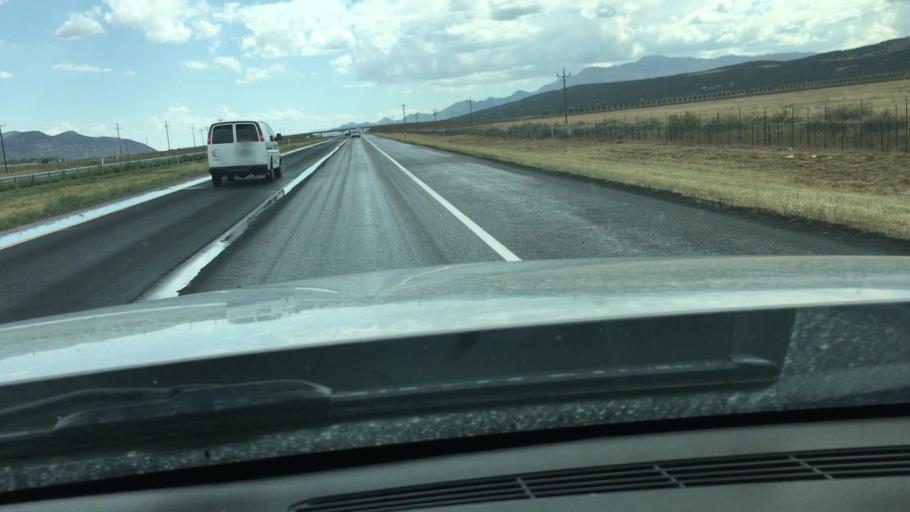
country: US
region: Utah
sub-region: Iron County
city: Cedar City
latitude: 37.5657
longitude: -113.1871
